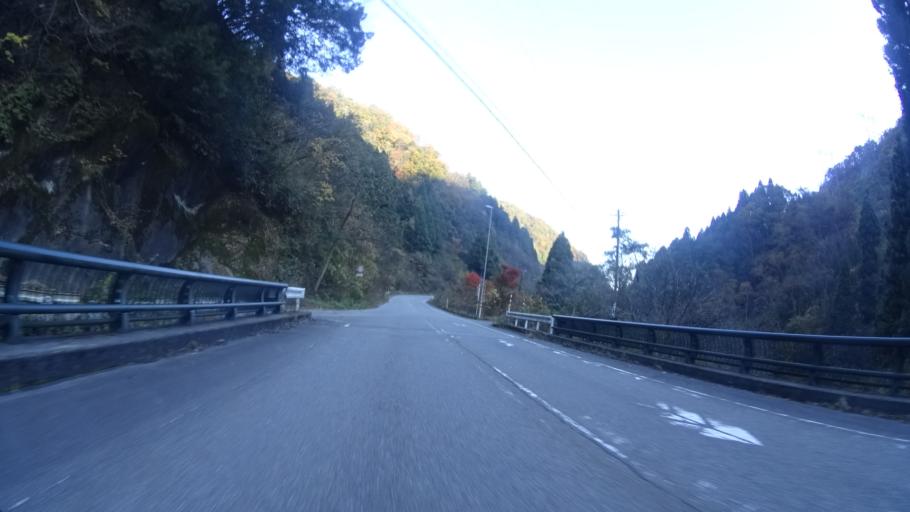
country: JP
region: Fukui
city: Maruoka
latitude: 36.1998
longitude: 136.3451
